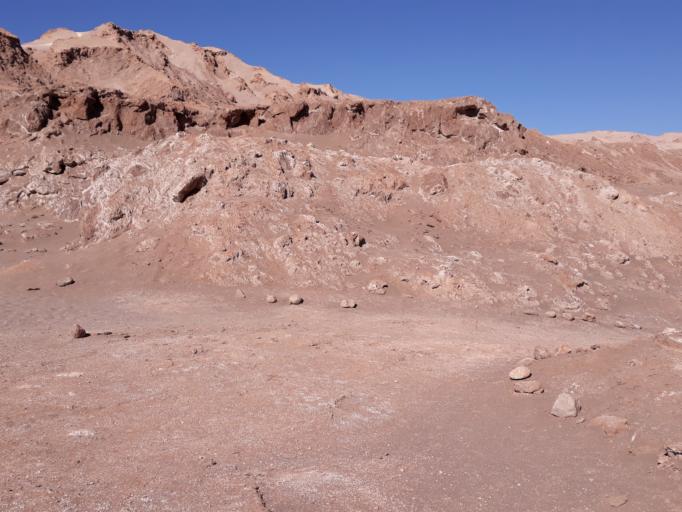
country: CL
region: Antofagasta
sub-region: Provincia de El Loa
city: San Pedro de Atacama
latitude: -22.9324
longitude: -68.3099
